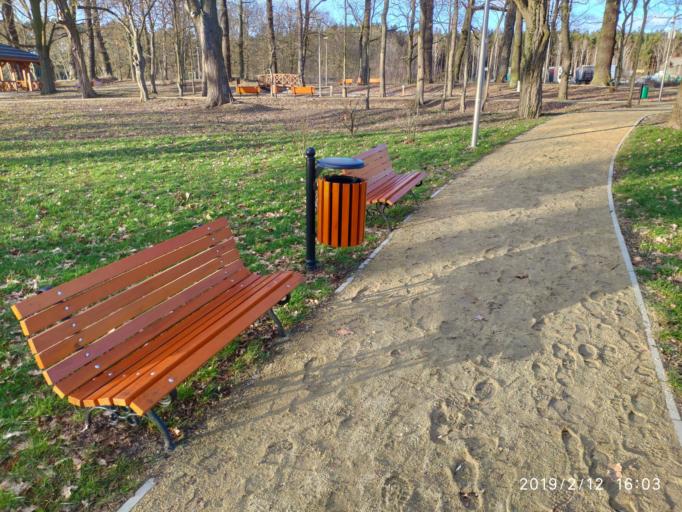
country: PL
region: Lubusz
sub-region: Powiat zielonogorski
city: Ochla
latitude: 51.8686
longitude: 15.5060
